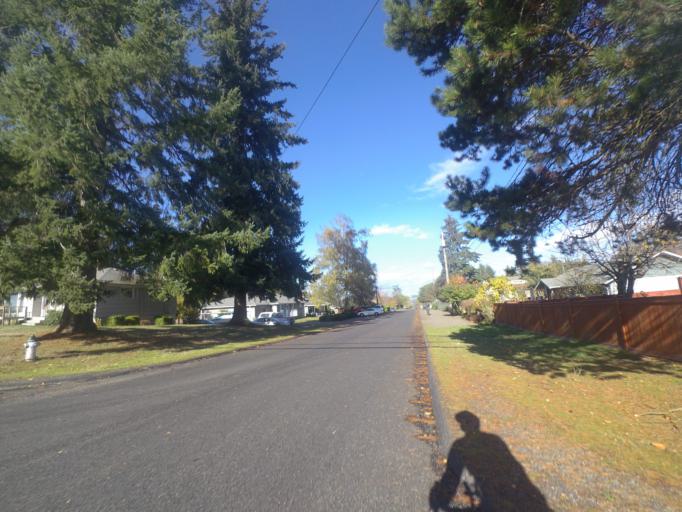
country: US
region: Washington
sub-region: Pierce County
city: University Place
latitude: 47.2299
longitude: -122.5530
